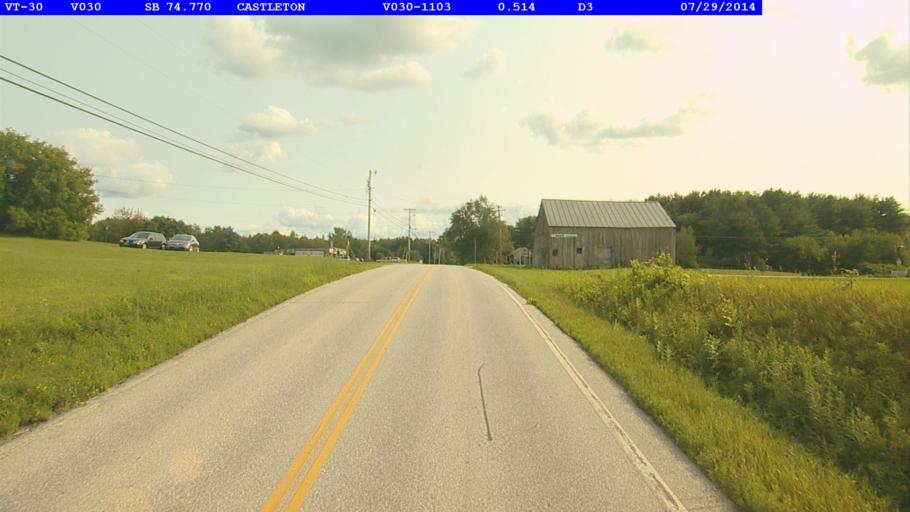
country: US
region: Vermont
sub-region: Rutland County
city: Castleton
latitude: 43.5941
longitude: -73.2093
